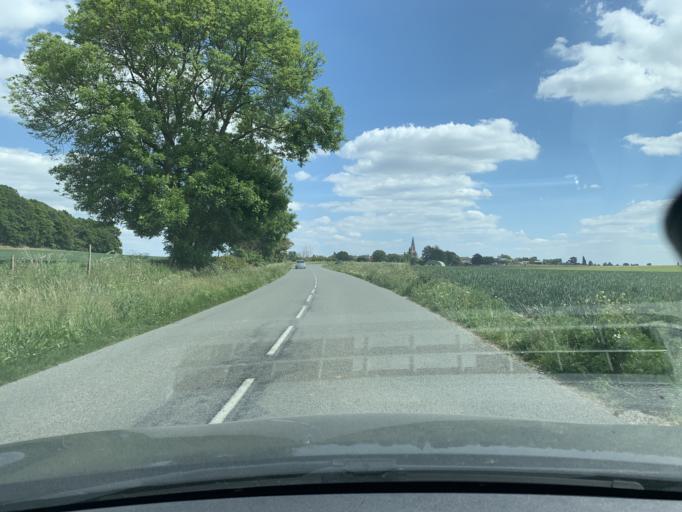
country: FR
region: Nord-Pas-de-Calais
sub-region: Departement du Pas-de-Calais
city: Oisy-le-Verger
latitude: 50.2573
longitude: 3.1081
